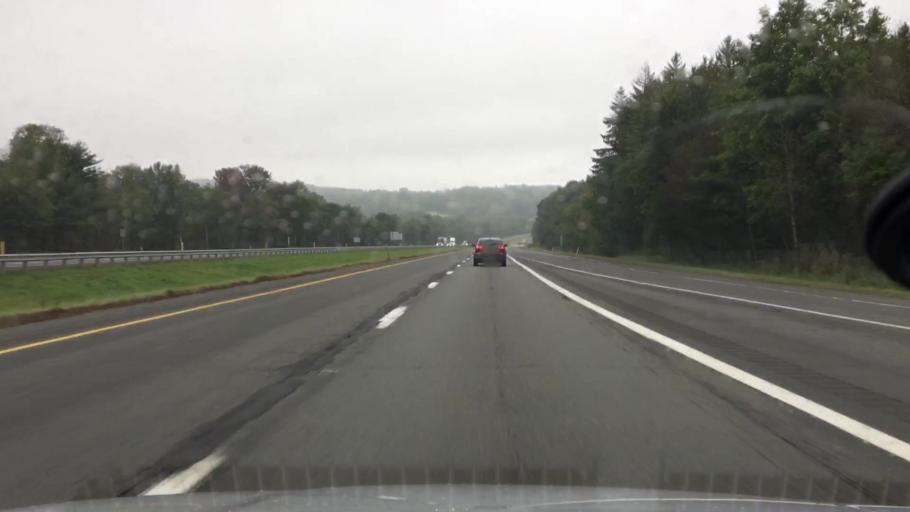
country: US
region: Pennsylvania
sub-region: Carbon County
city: Towamensing Trails
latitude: 41.0769
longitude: -75.5816
